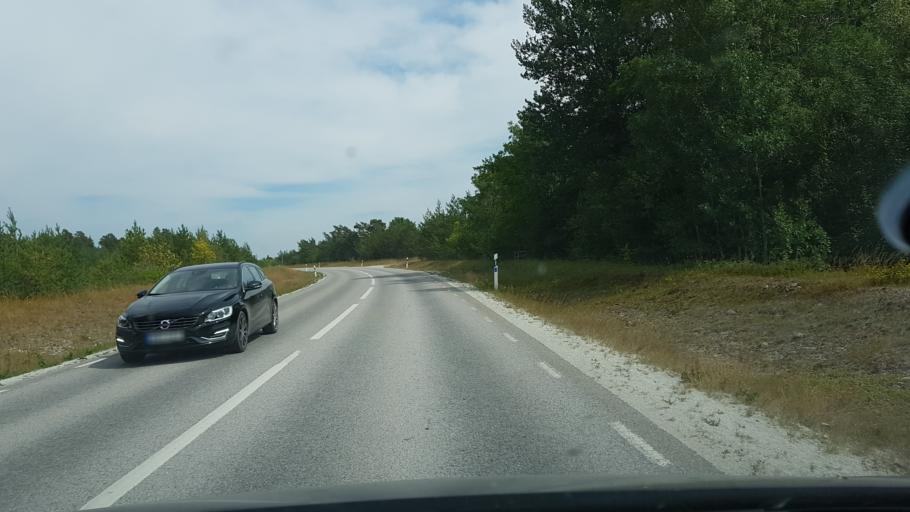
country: SE
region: Gotland
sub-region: Gotland
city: Slite
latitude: 57.7439
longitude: 18.6424
